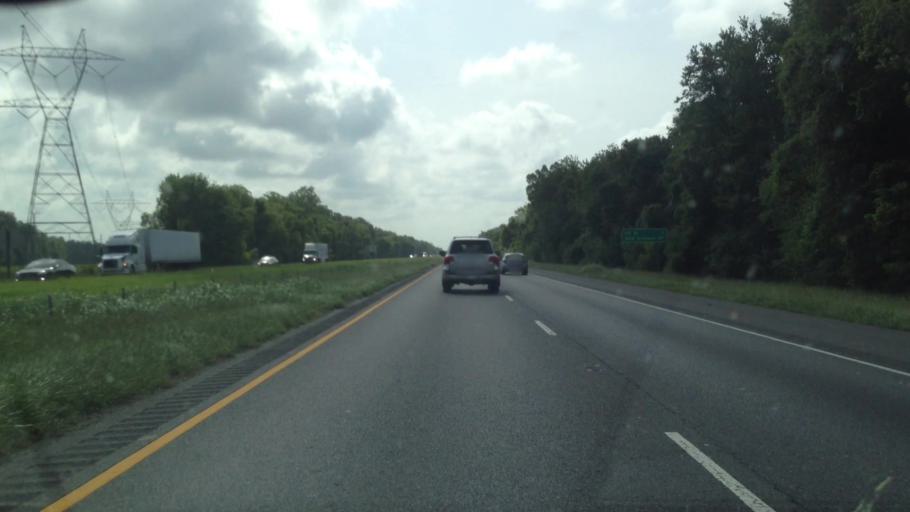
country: US
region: Louisiana
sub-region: Ascension Parish
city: Sorrento
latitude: 30.1672
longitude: -90.8618
